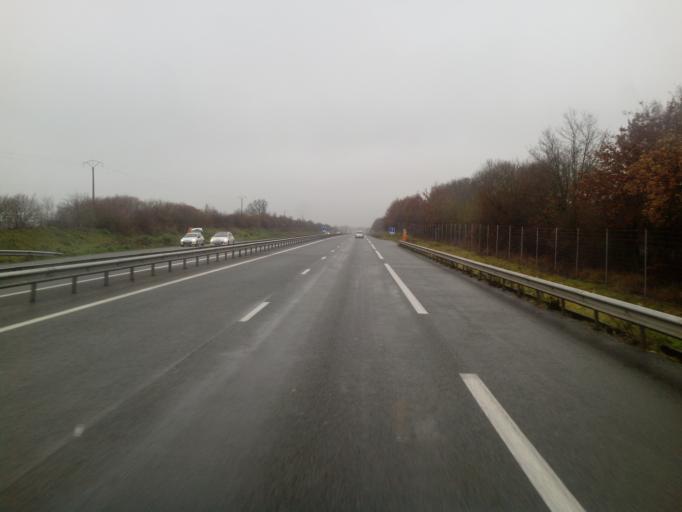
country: FR
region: Poitou-Charentes
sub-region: Departement de la Vienne
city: Savigny-Levescault
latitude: 46.5000
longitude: 0.4850
